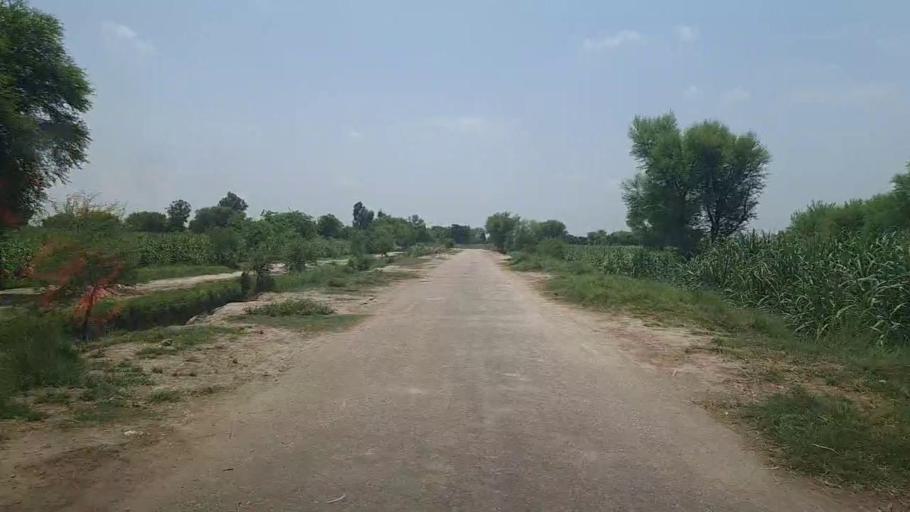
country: PK
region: Sindh
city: Ubauro
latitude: 28.2809
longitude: 69.8086
